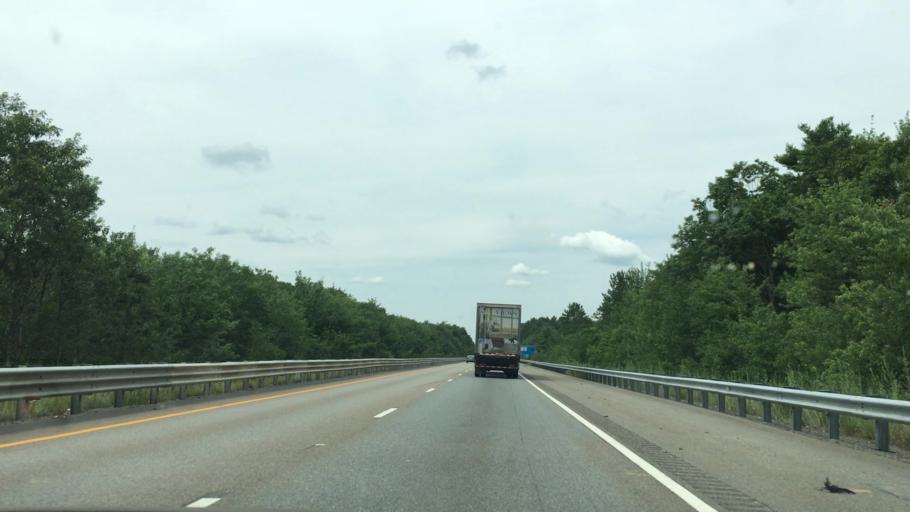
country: US
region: Massachusetts
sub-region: Worcester County
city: Gardner
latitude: 42.5619
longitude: -71.9592
